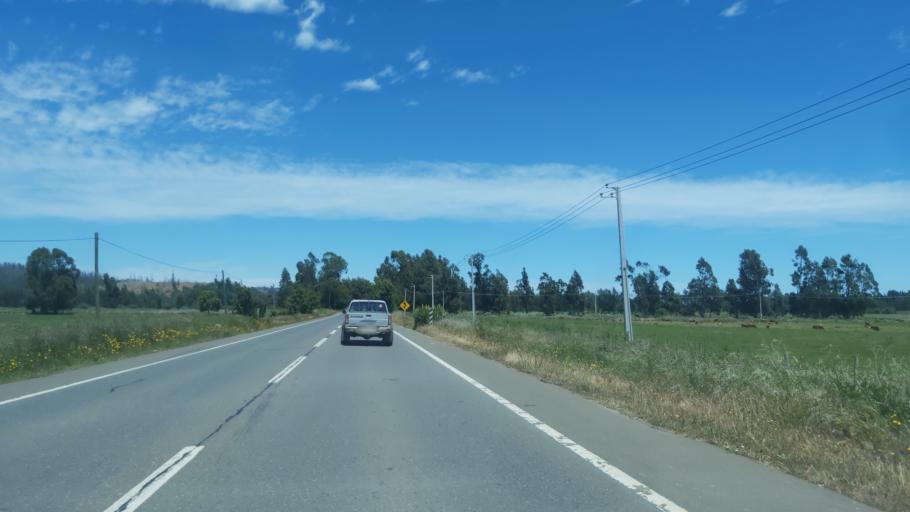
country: CL
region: Maule
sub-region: Provincia de Talca
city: Constitucion
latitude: -35.2966
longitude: -72.3701
